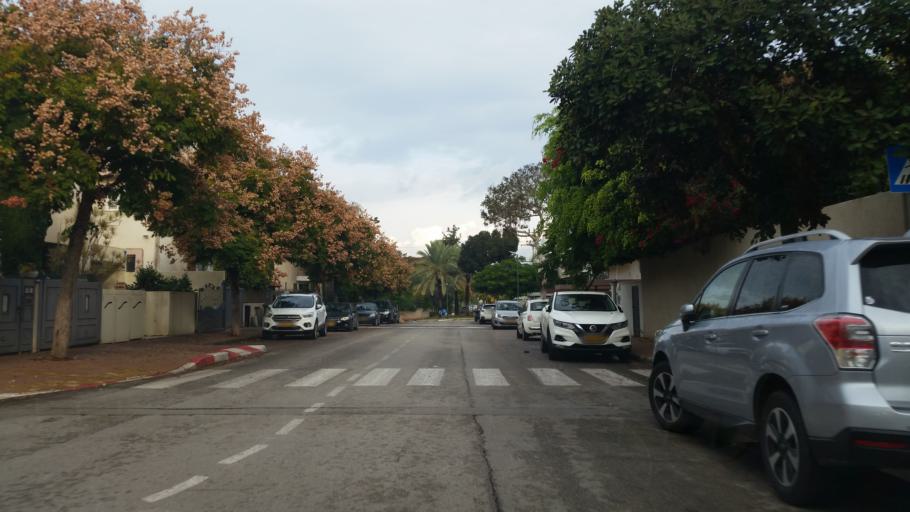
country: IL
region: Tel Aviv
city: Ramat HaSharon
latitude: 32.1528
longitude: 34.8479
